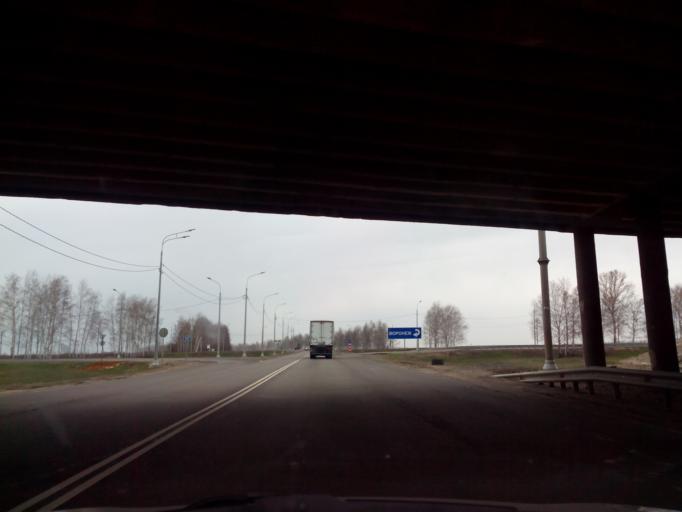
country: RU
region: Tambov
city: Pokrovo-Prigorodnoye
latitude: 52.6610
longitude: 41.3398
